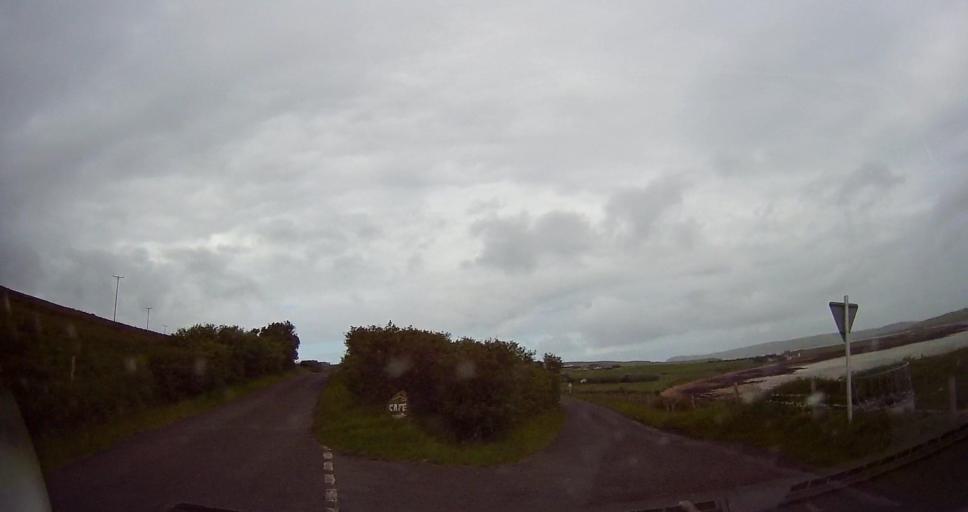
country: GB
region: Scotland
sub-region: Orkney Islands
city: Stromness
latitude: 58.9059
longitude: -3.3161
